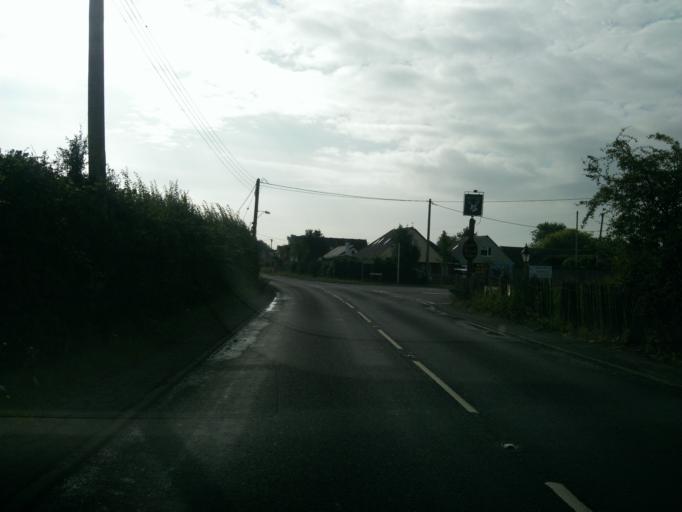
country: GB
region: England
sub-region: Essex
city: Little Clacton
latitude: 51.8448
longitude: 1.1231
